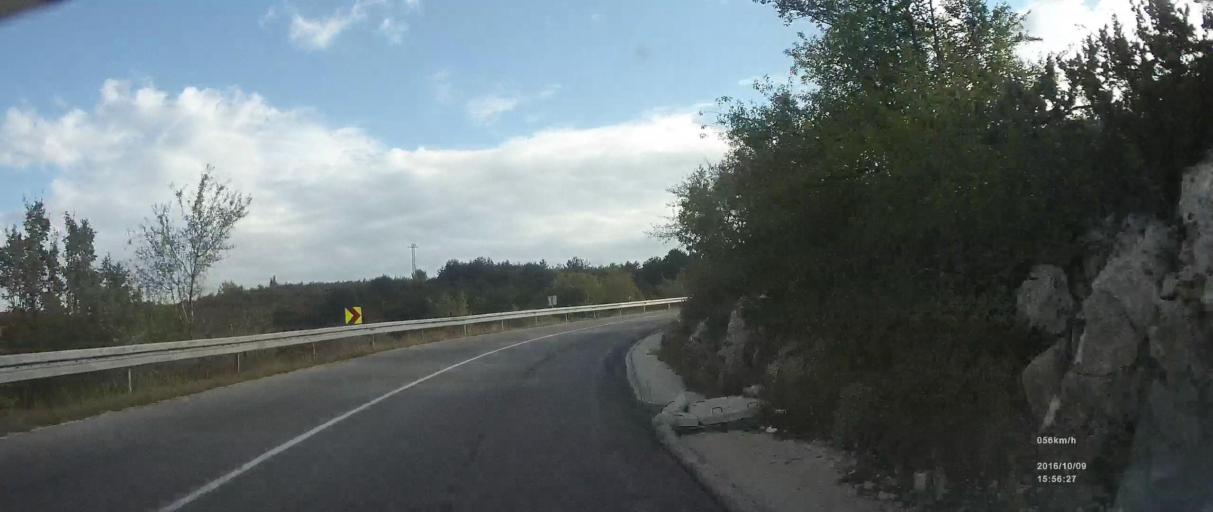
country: HR
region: Splitsko-Dalmatinska
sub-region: Grad Trogir
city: Trogir
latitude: 43.5784
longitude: 16.2336
